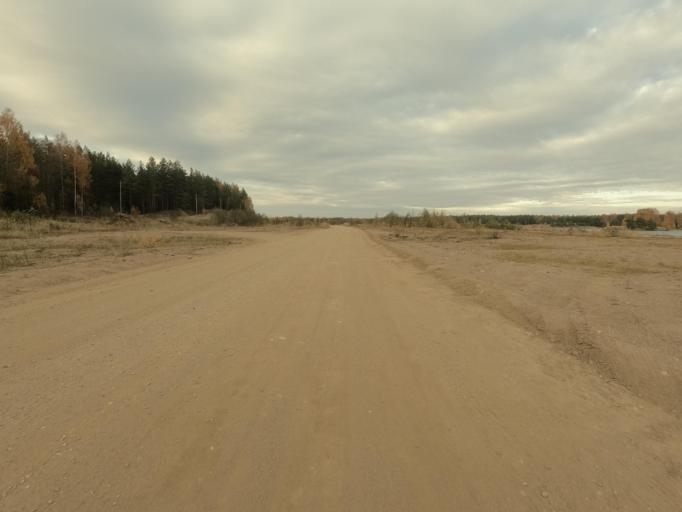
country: RU
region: Leningrad
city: Priladozhskiy
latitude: 59.7027
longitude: 31.3630
